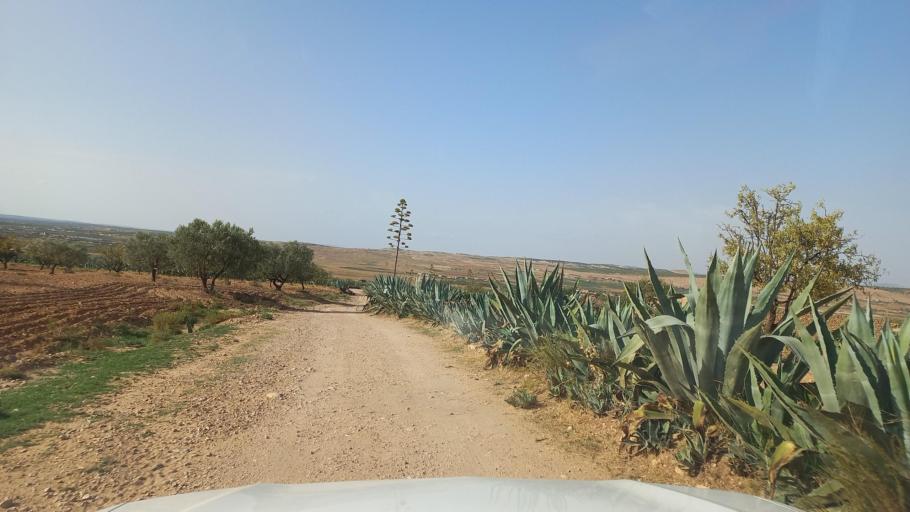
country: TN
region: Al Qasrayn
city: Kasserine
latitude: 35.3348
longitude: 8.8456
